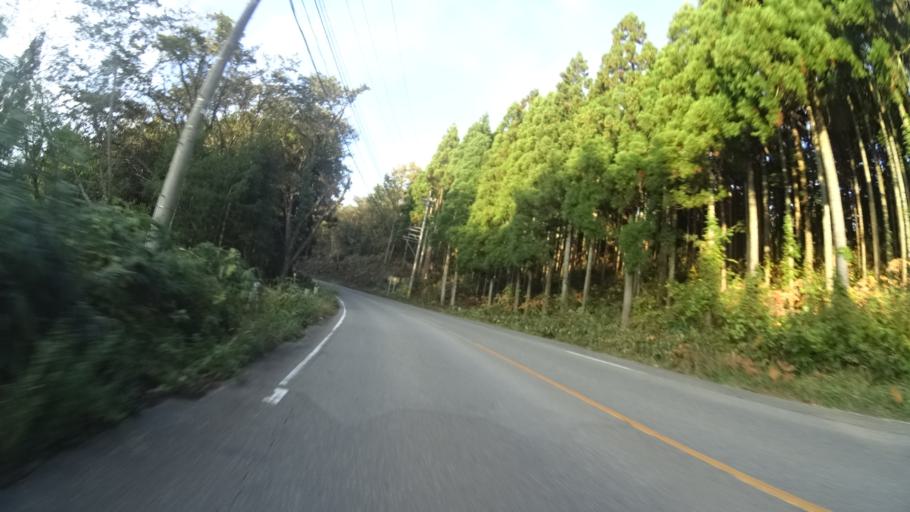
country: JP
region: Ishikawa
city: Nanao
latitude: 37.1677
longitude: 136.7146
